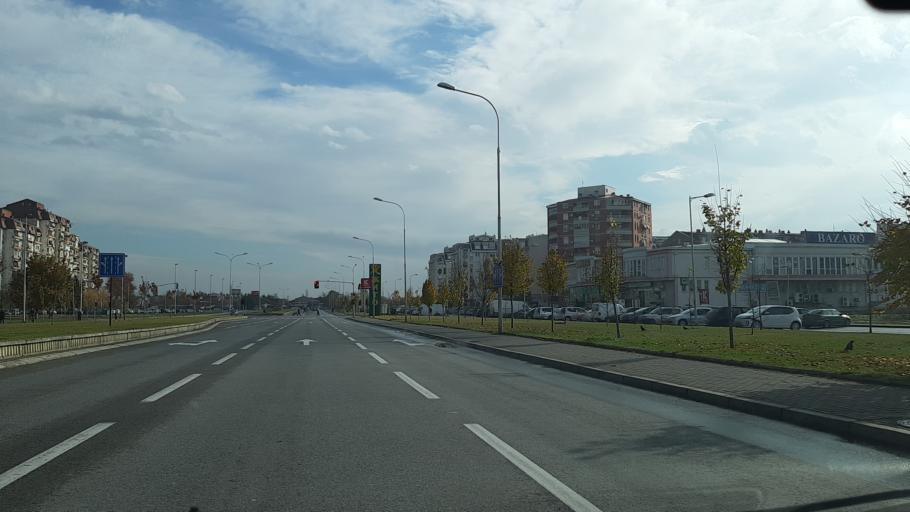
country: MK
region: Kisela Voda
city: Usje
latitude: 41.9810
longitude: 21.4747
